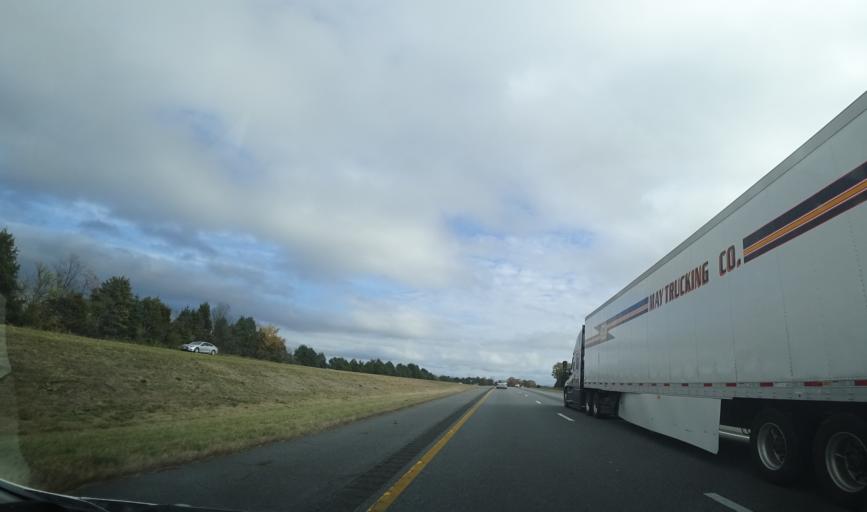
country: US
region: Virginia
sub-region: Frederick County
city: Middletown
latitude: 38.9954
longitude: -78.2584
